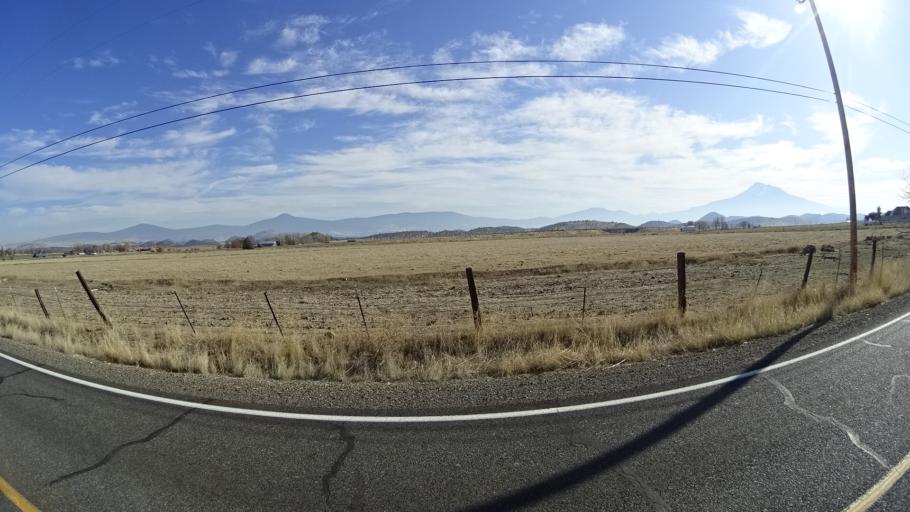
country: US
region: California
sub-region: Siskiyou County
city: Montague
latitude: 41.6299
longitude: -122.5297
